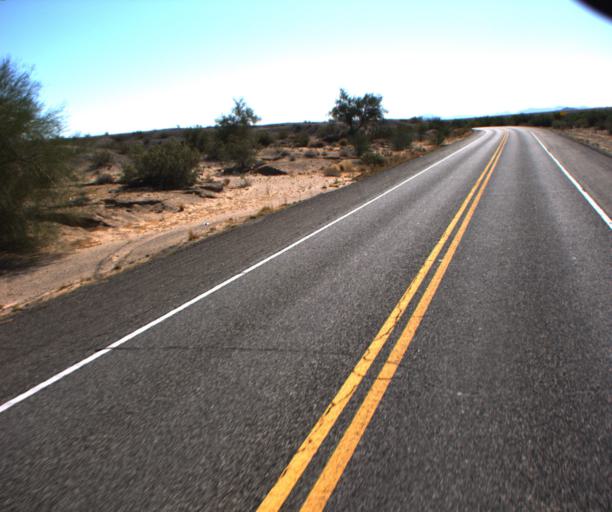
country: US
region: Arizona
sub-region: La Paz County
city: Parker
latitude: 33.9935
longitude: -114.2118
